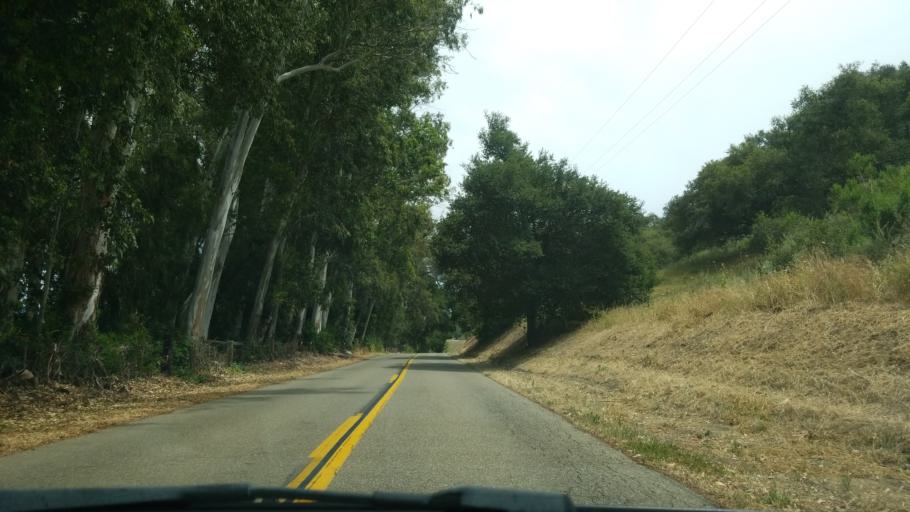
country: US
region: California
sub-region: Santa Barbara County
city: Los Olivos
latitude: 34.7800
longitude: -120.1591
